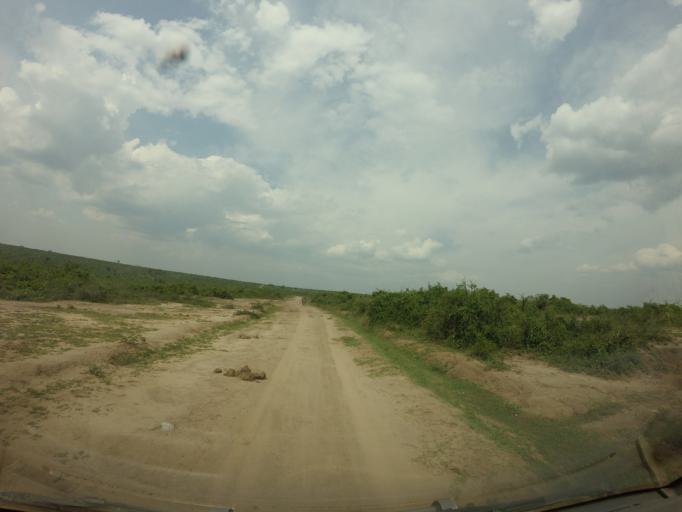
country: UG
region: Western Region
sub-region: Rubirizi District
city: Rubirizi
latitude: -0.2100
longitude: 29.9069
